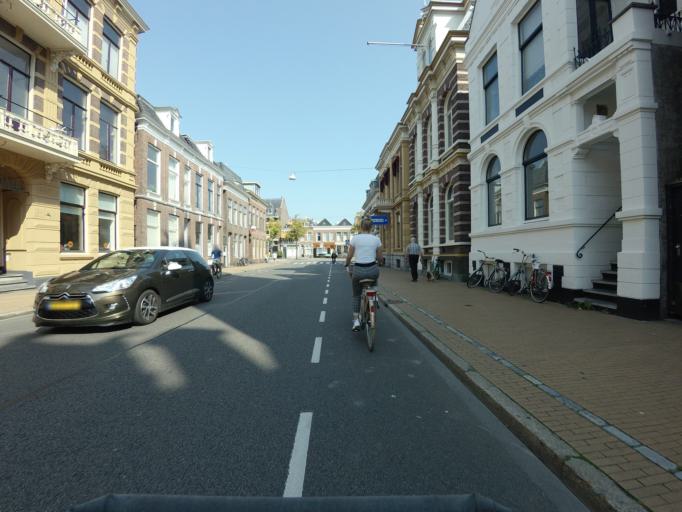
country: NL
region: Groningen
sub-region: Gemeente Groningen
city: Groningen
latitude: 53.2141
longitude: 6.5626
